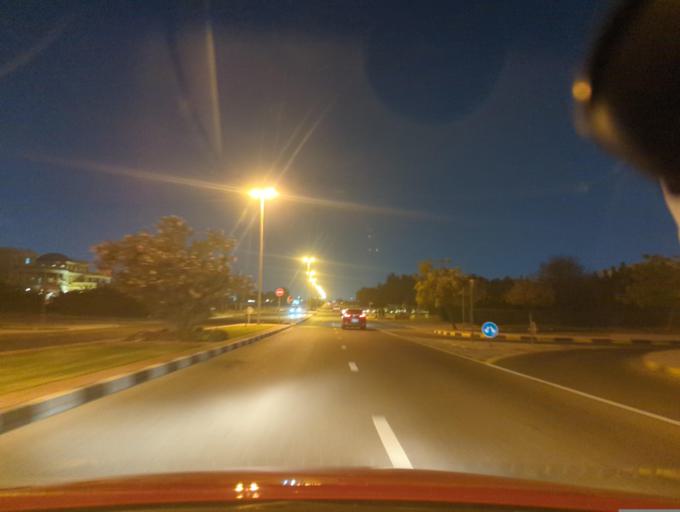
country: AE
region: Ash Shariqah
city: Sharjah
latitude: 25.3439
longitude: 55.4705
